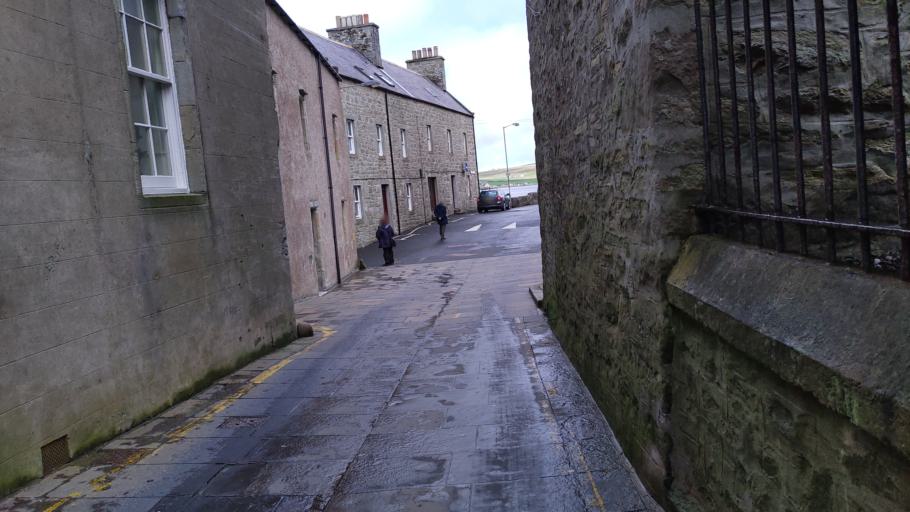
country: GB
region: Scotland
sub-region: Shetland Islands
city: Shetland
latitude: 60.1526
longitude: -1.1380
